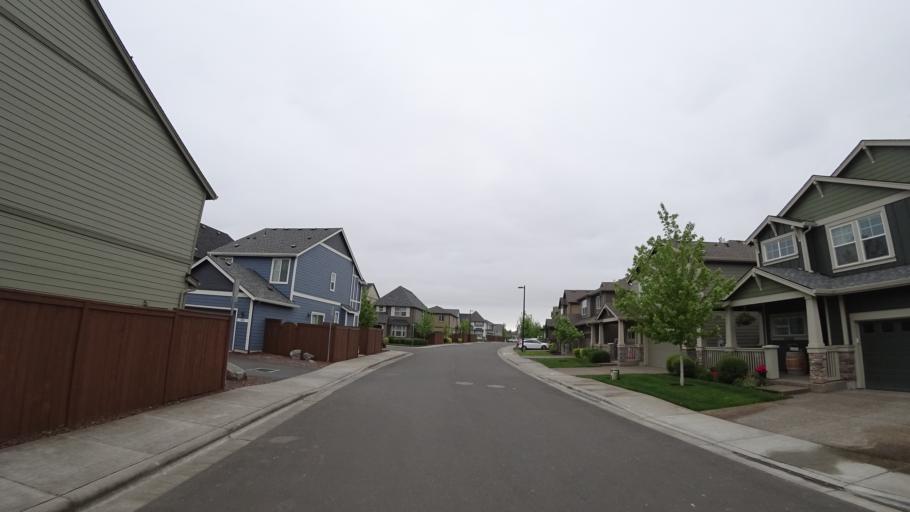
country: US
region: Oregon
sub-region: Washington County
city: Aloha
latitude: 45.5168
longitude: -122.8812
